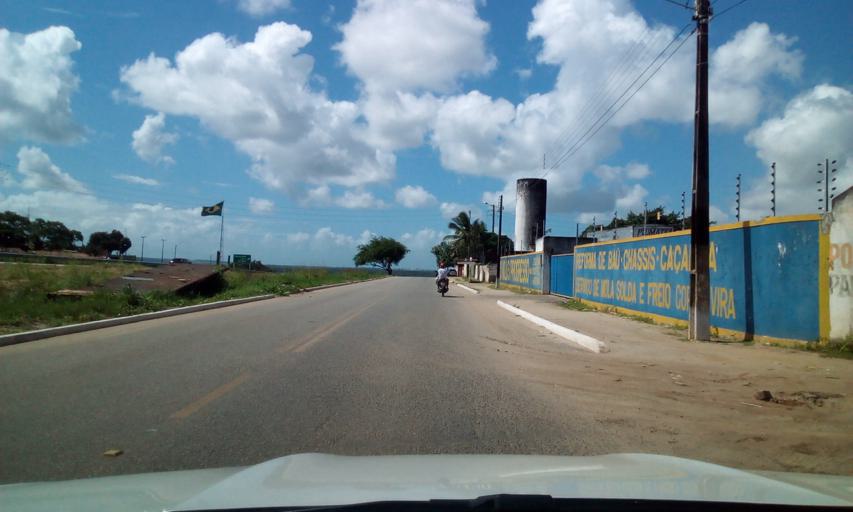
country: BR
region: Paraiba
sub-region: Bayeux
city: Bayeux
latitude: -7.1278
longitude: -34.9508
